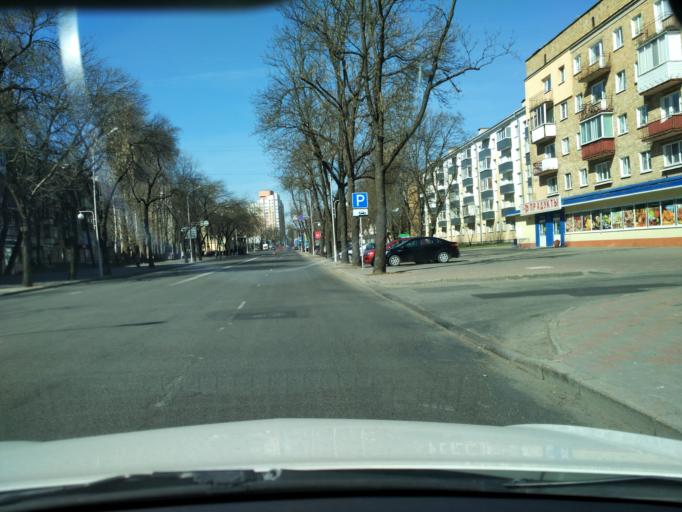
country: BY
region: Minsk
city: Minsk
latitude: 53.8738
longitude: 27.5351
